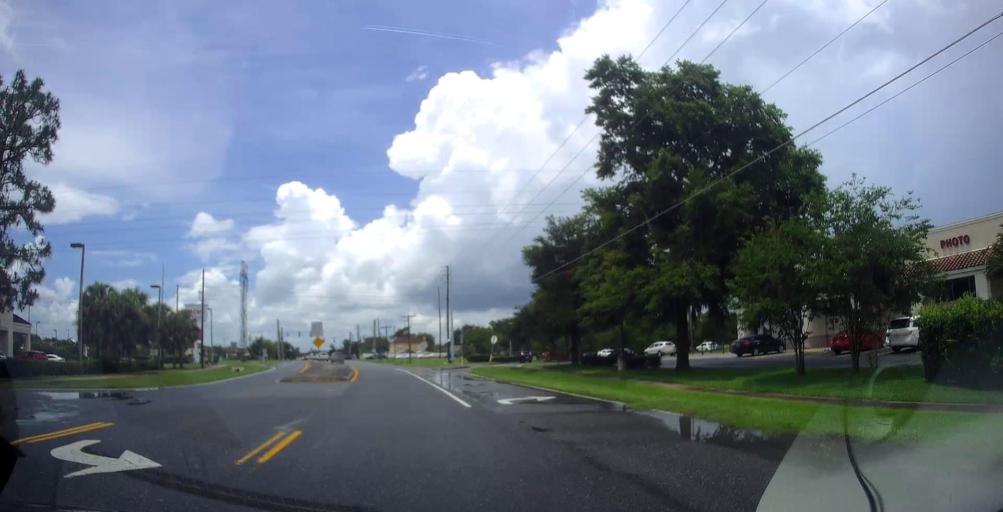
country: US
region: Florida
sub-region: Marion County
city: Silver Springs Shores
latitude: 29.1195
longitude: -82.0262
